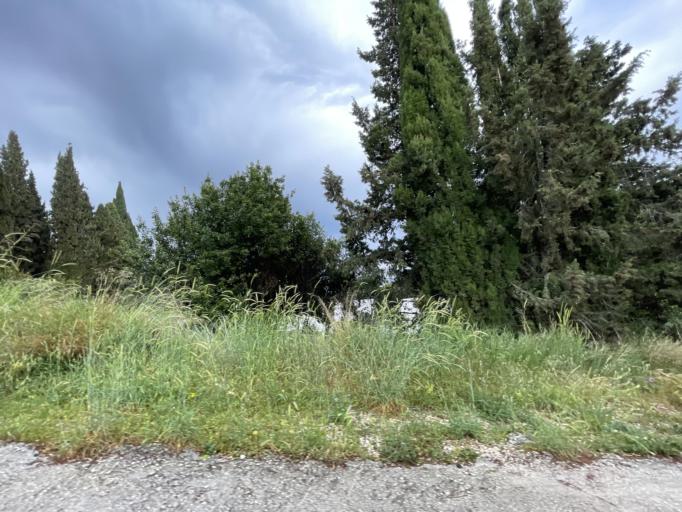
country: HR
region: Splitsko-Dalmatinska
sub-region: Grad Split
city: Split
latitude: 43.5050
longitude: 16.4031
